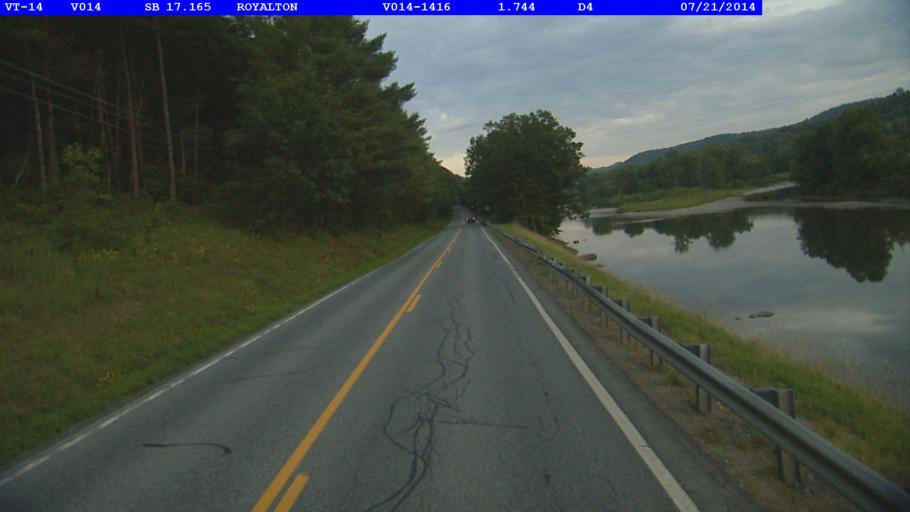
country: US
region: Vermont
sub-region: Orange County
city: Chelsea
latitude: 43.8175
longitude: -72.5107
